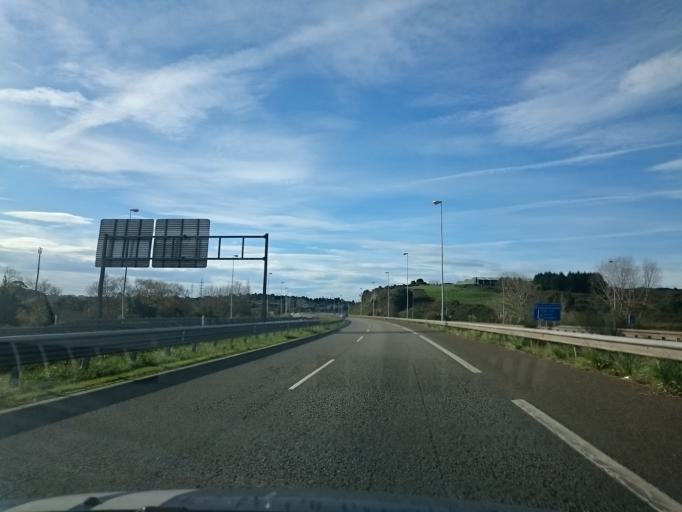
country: ES
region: Asturias
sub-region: Province of Asturias
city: Natahoyo
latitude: 43.5193
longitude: -5.7004
